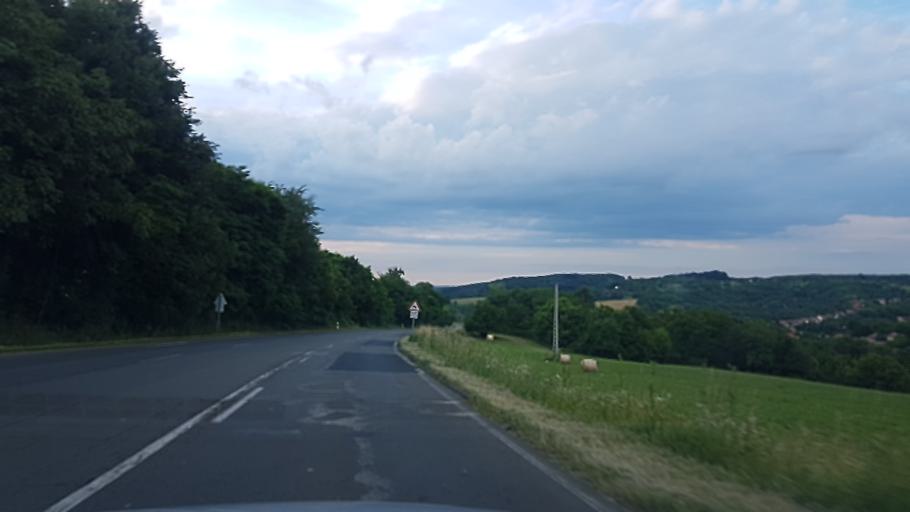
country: HU
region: Somogy
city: Kaposvar
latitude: 46.2756
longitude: 17.8217
